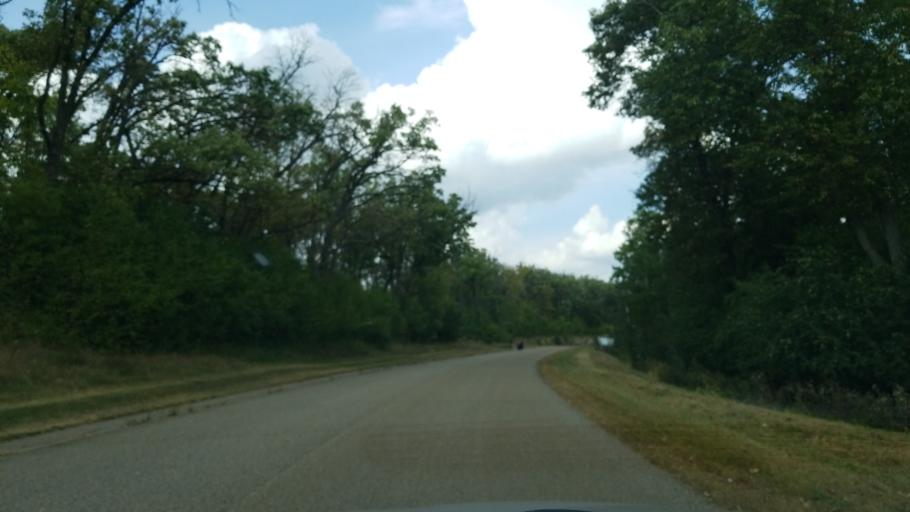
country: US
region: Minnesota
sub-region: Washington County
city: Lake Saint Croix Beach
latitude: 44.9056
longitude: -92.7413
